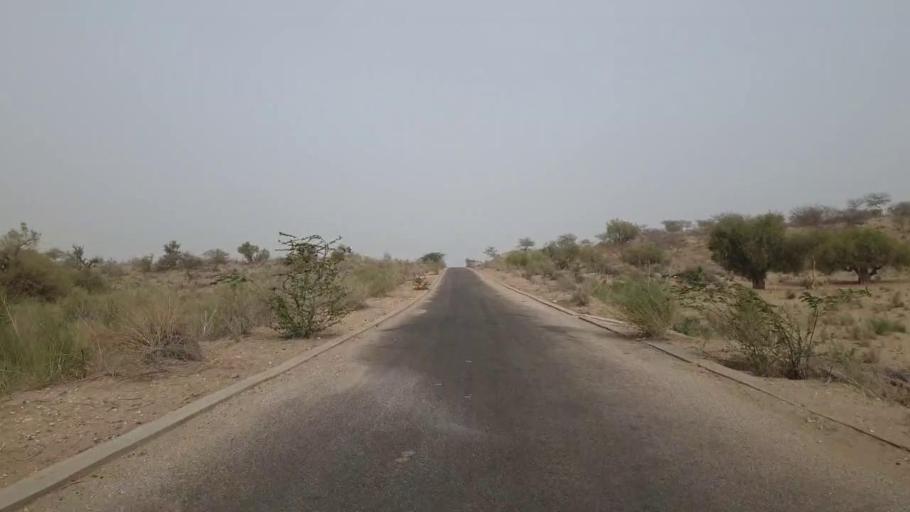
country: PK
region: Sindh
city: Islamkot
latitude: 24.5873
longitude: 70.2928
